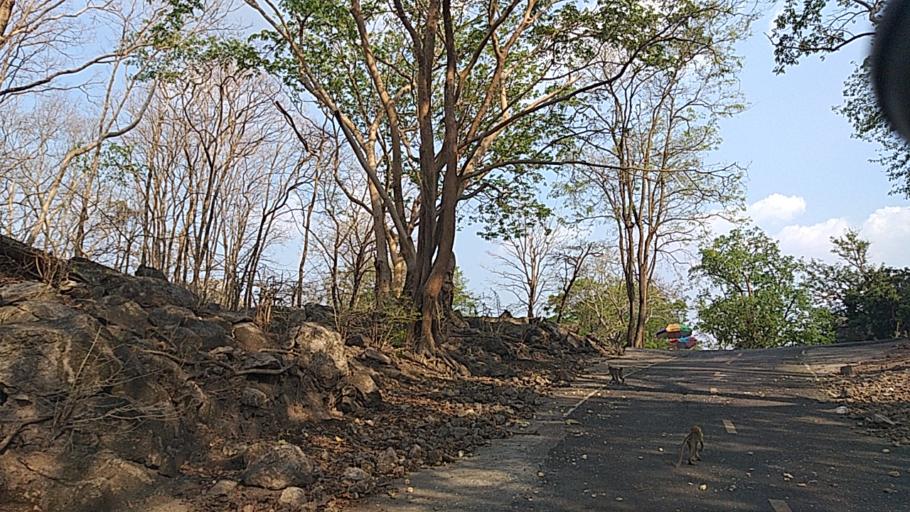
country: TH
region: Sara Buri
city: Saraburi
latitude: 14.4621
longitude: 100.9496
